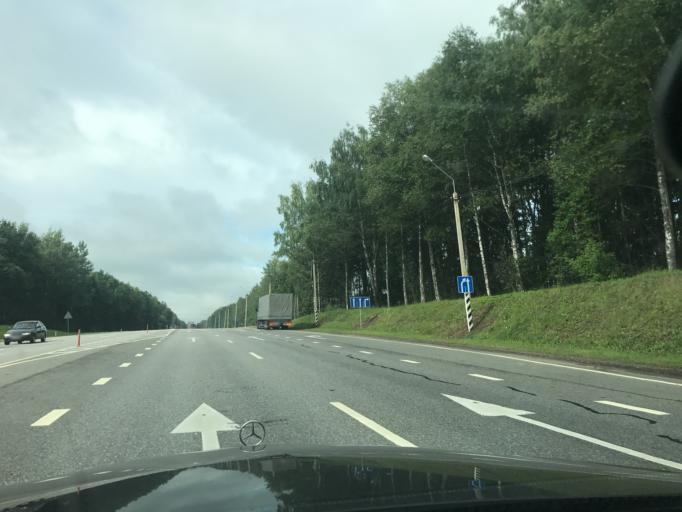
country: RU
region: Smolensk
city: Kardymovo
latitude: 55.0101
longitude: 32.2893
